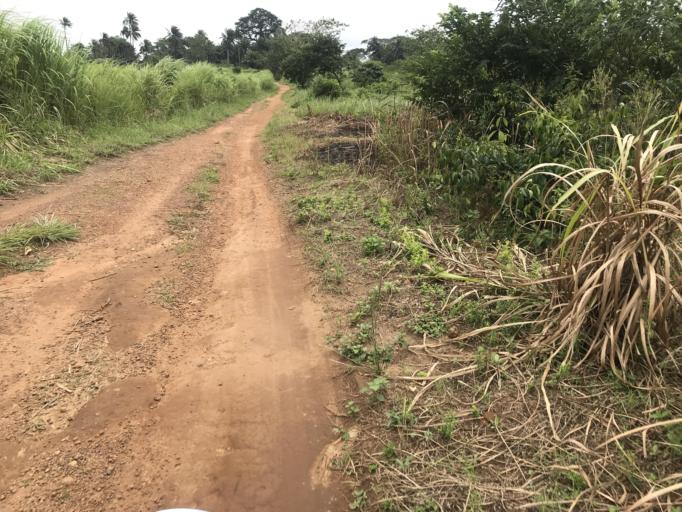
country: SL
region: Eastern Province
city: Buedu
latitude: 8.4742
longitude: -10.3165
